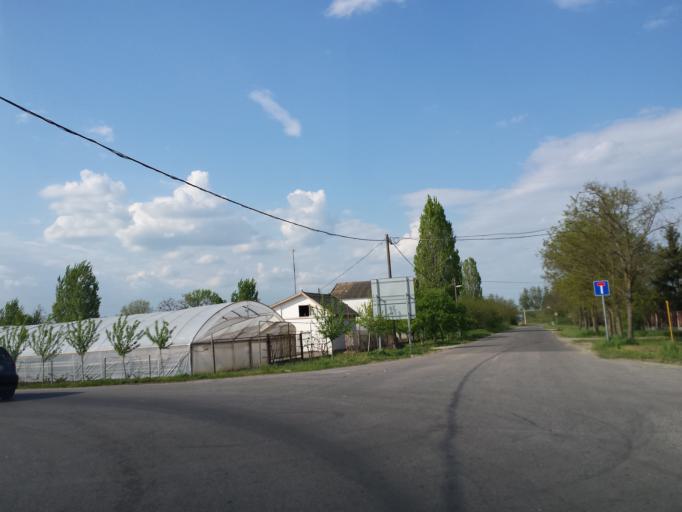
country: HU
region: Csongrad
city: Mako
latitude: 46.2399
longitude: 20.4839
